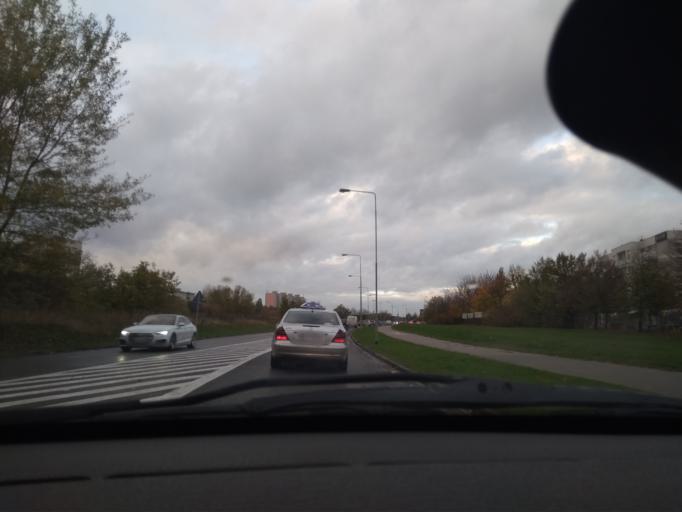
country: PL
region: Greater Poland Voivodeship
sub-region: Powiat poznanski
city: Suchy Las
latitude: 52.4567
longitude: 16.9183
